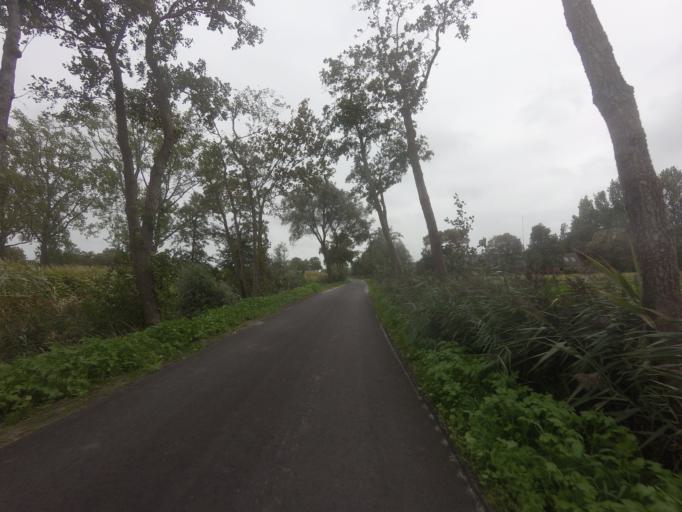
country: NL
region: Friesland
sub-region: Gemeente Leeuwarden
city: Bilgaard
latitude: 53.2318
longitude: 5.7811
